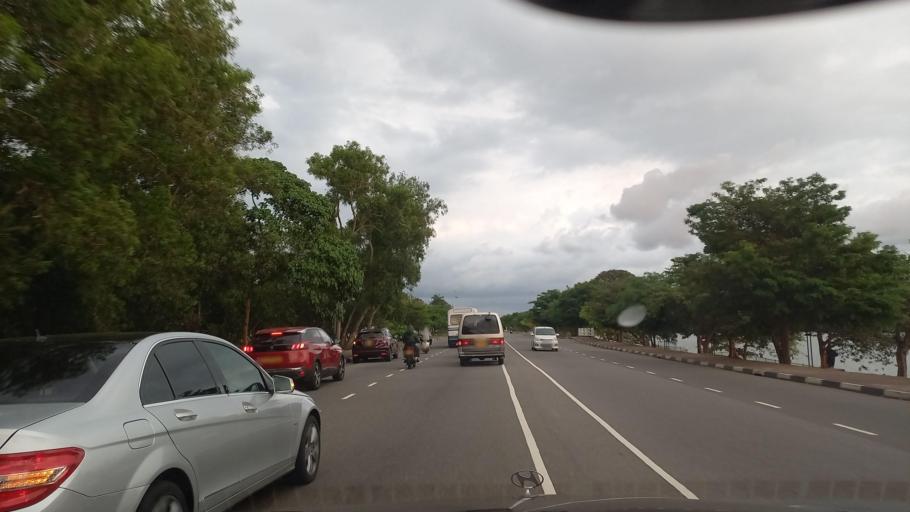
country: LK
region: Western
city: Battaramulla South
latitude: 6.8883
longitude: 79.9218
